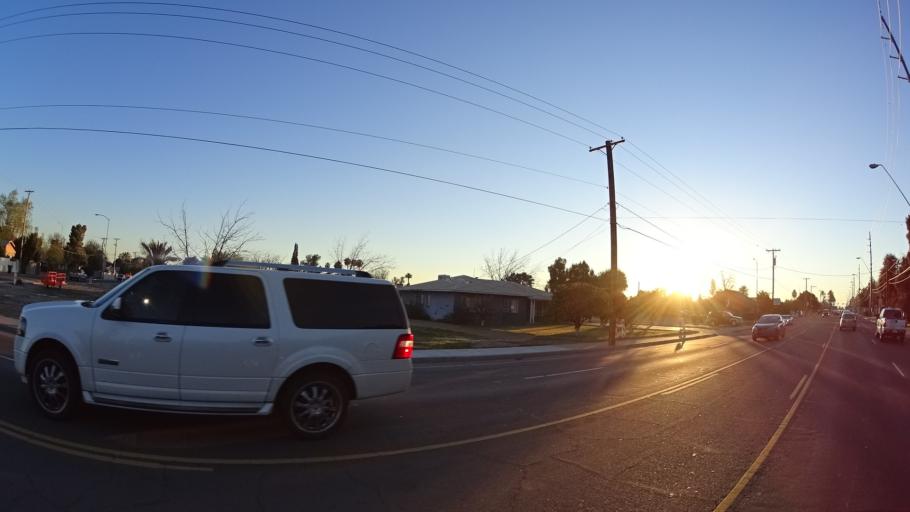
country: US
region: Arizona
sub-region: Maricopa County
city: Mesa
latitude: 33.4224
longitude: -111.8442
